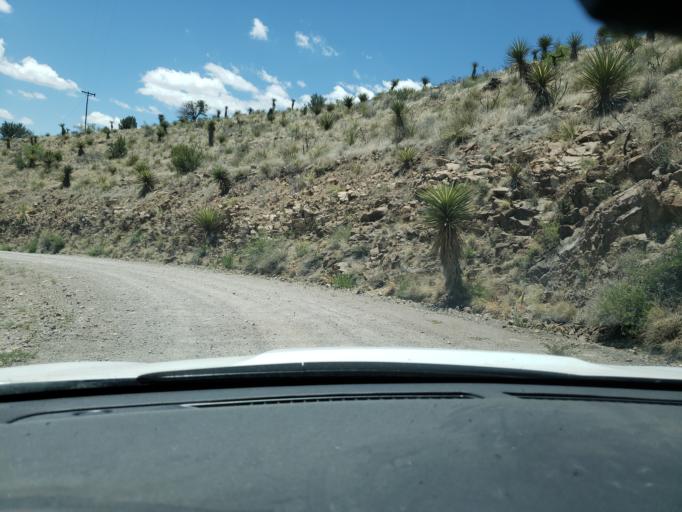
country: MX
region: Chihuahua
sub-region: Ojinaga
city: Manuel Ojinaga
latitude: 30.0419
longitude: -104.4691
